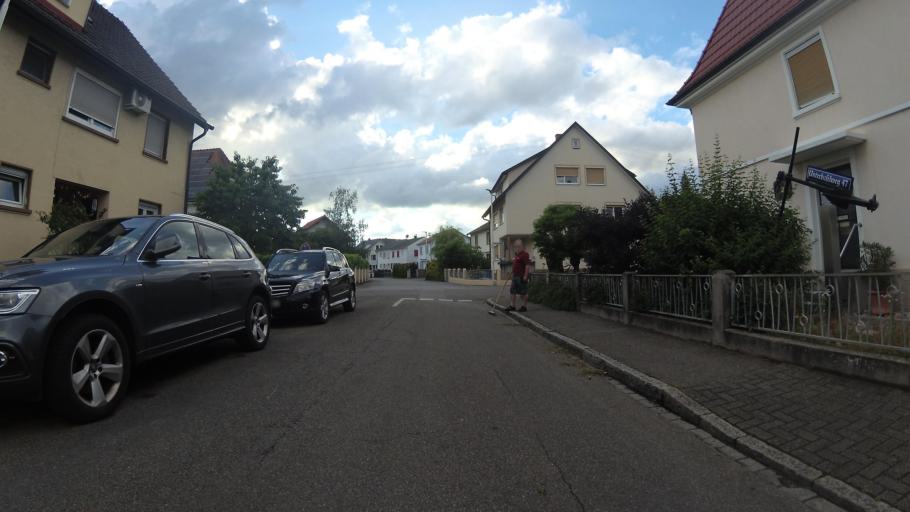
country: DE
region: Baden-Wuerttemberg
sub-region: Freiburg Region
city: Weil am Rhein
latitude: 47.5906
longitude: 7.6248
